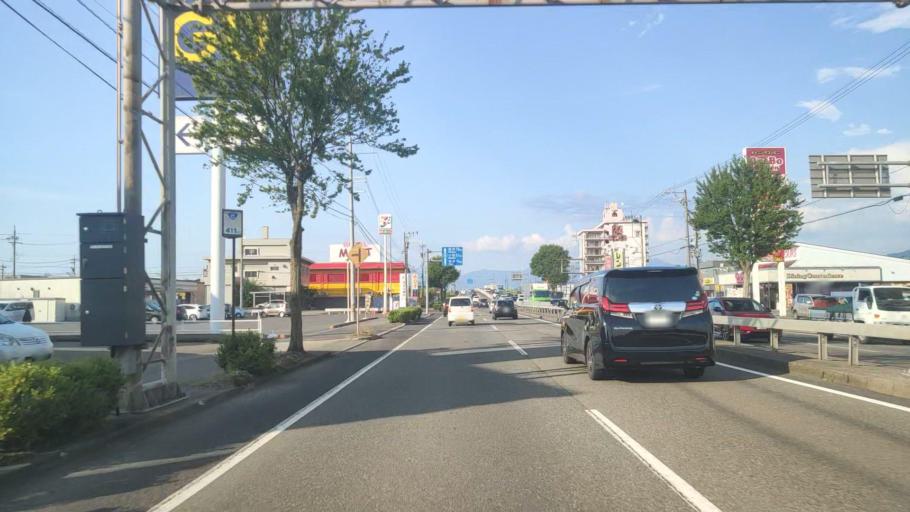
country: JP
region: Fukui
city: Fukui-shi
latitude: 36.0440
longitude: 136.2351
